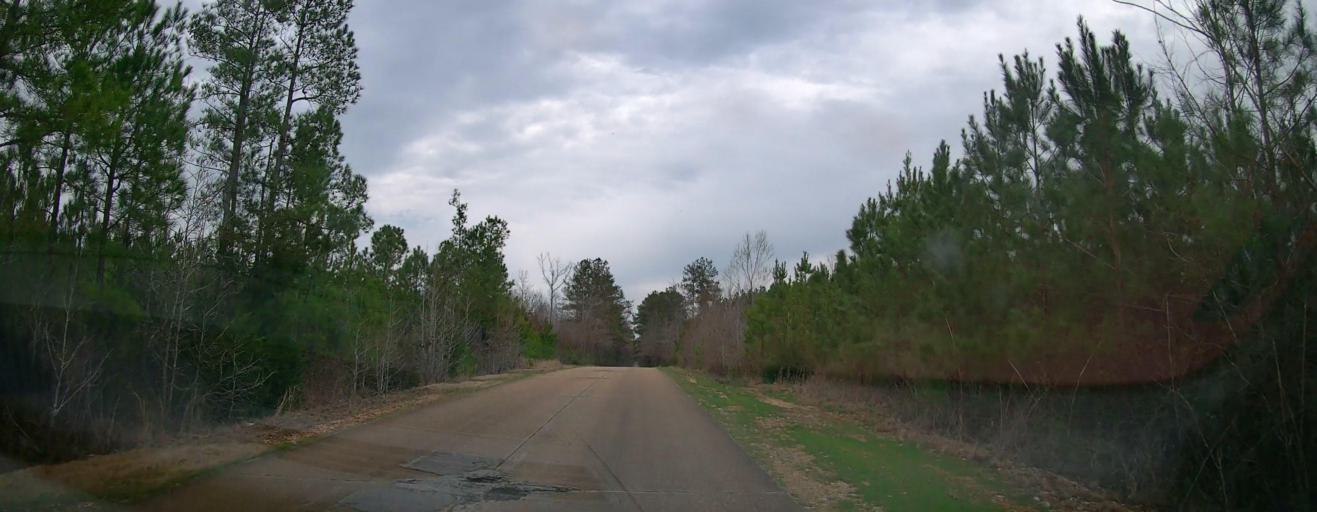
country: US
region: Alabama
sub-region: Marion County
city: Hamilton
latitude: 34.2106
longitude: -88.1980
